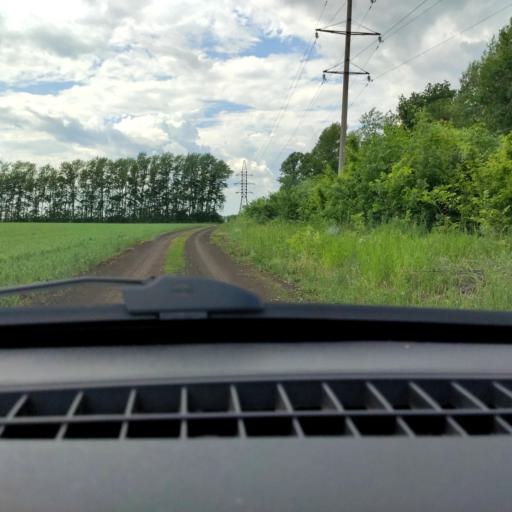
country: RU
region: Bashkortostan
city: Kabakovo
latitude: 54.5180
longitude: 56.0848
